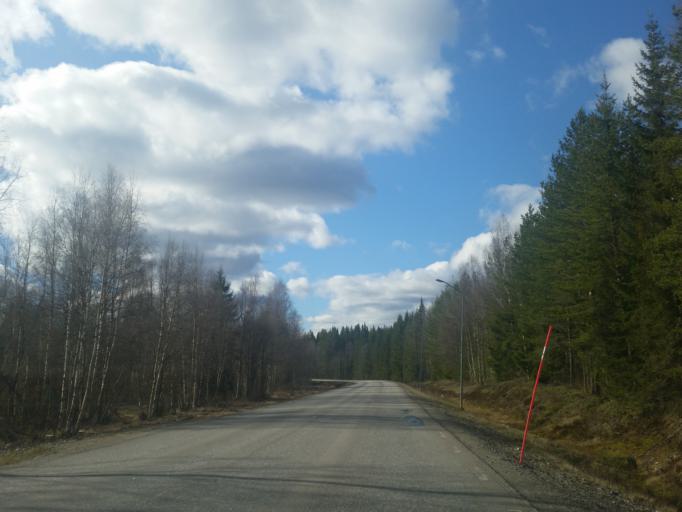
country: SE
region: Vaesterbotten
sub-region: Robertsfors Kommun
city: Robertsfors
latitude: 64.1998
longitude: 20.8325
